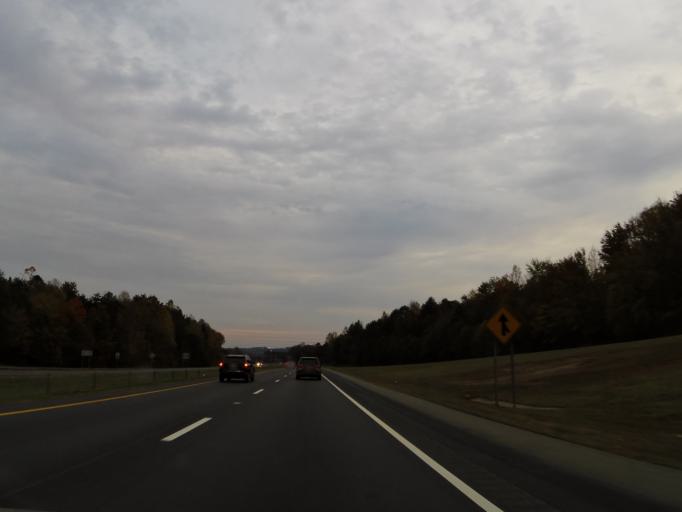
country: US
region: North Carolina
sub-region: Catawba County
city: Hickory
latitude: 35.7203
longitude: -81.3562
